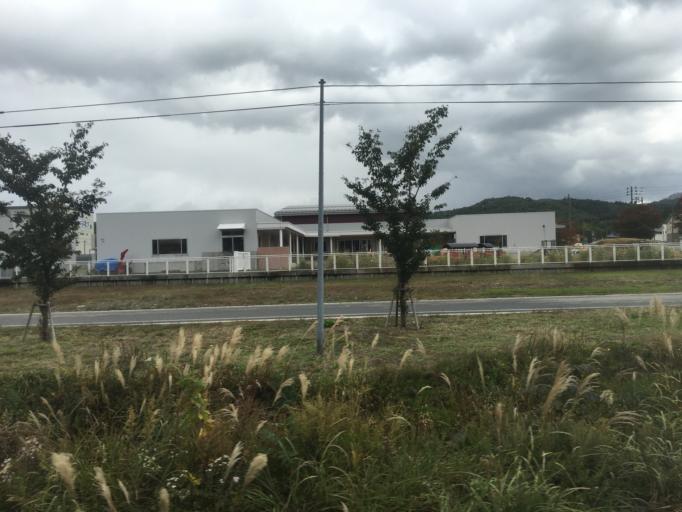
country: JP
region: Yamagata
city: Nagai
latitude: 38.0599
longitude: 139.7514
